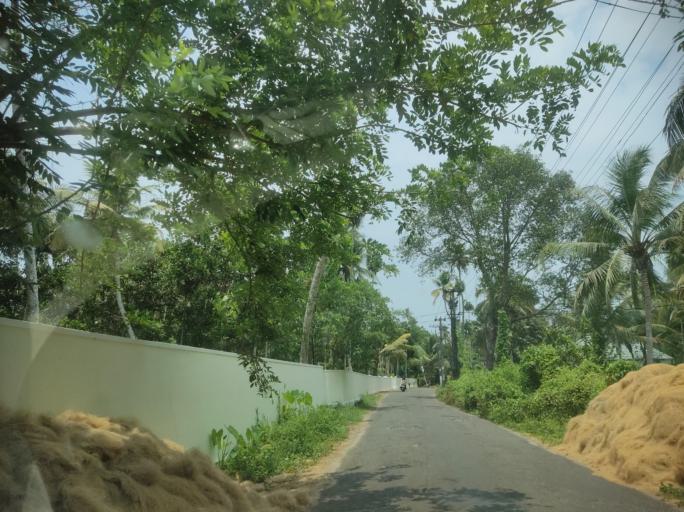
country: IN
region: Kerala
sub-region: Alappuzha
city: Vayalar
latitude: 9.7470
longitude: 76.3249
